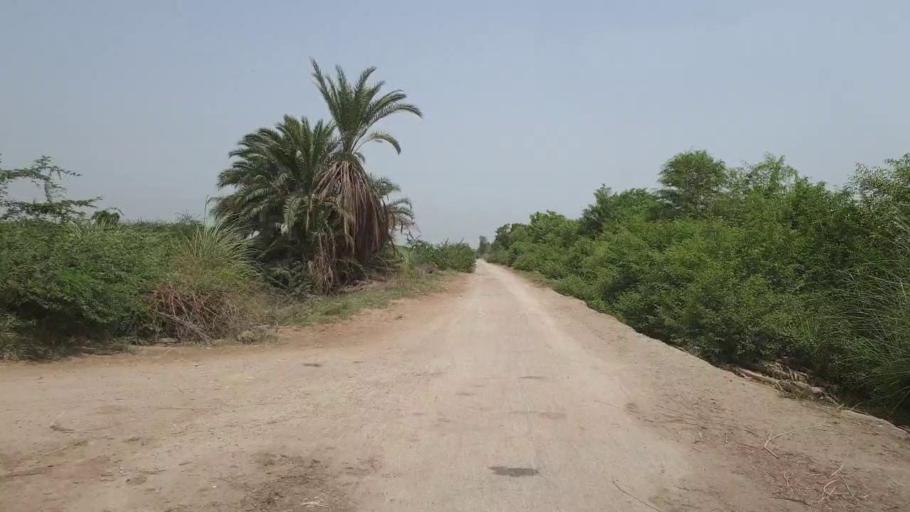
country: PK
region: Sindh
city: Nawabshah
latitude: 26.3021
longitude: 68.3045
